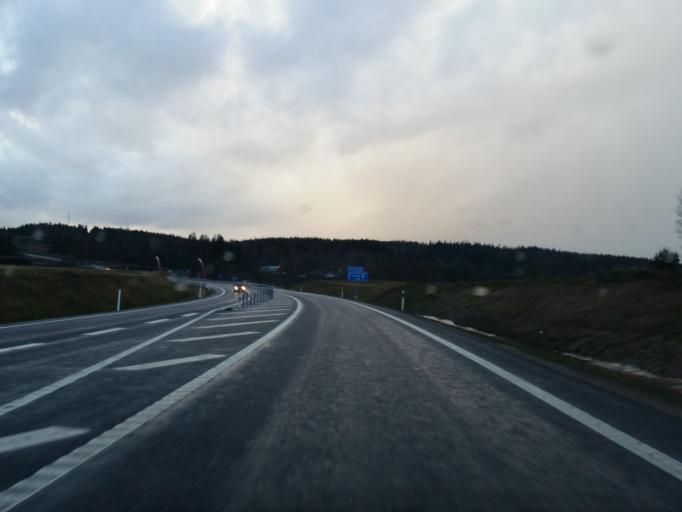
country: SE
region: Vaestra Goetaland
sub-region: Boras Kommun
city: Boras
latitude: 57.6954
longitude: 12.9174
